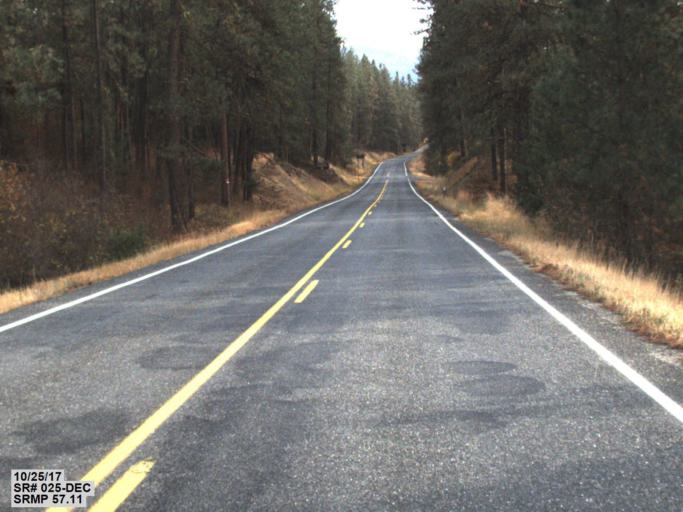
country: US
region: Washington
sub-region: Stevens County
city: Kettle Falls
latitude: 48.2988
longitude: -118.1464
